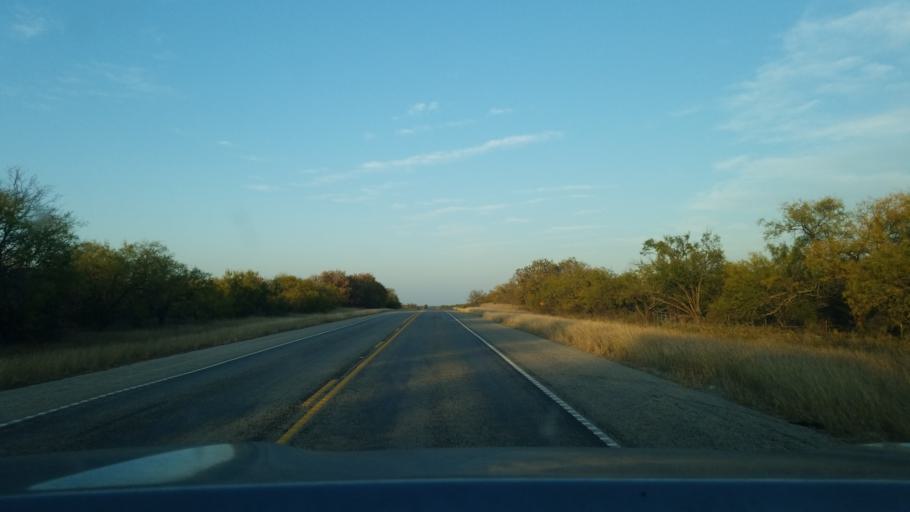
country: US
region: Texas
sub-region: Eastland County
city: Cisco
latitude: 32.4291
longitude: -98.9284
